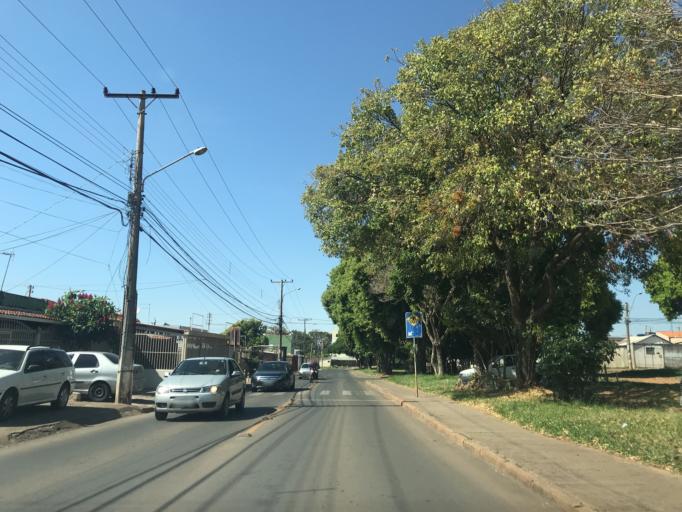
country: BR
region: Federal District
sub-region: Brasilia
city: Brasilia
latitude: -15.8159
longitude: -48.0807
